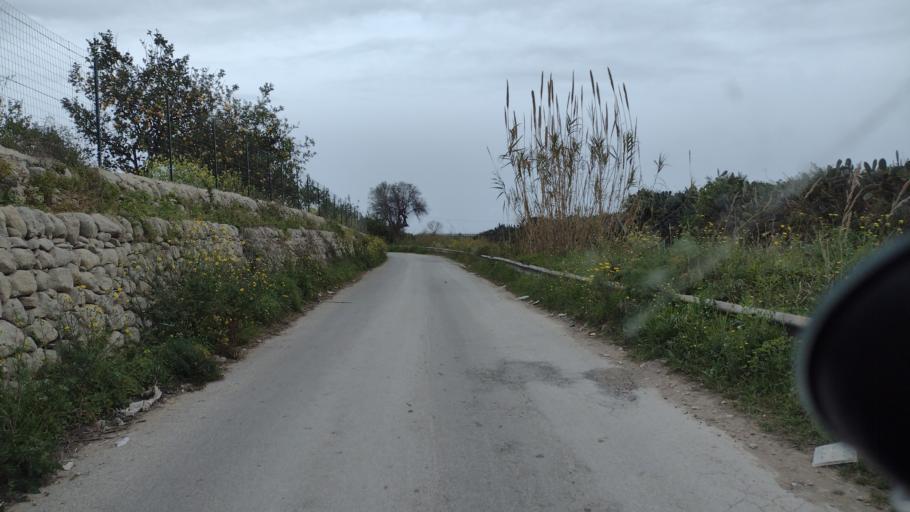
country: IT
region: Sicily
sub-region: Provincia di Siracusa
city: Avola
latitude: 36.9109
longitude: 15.1163
